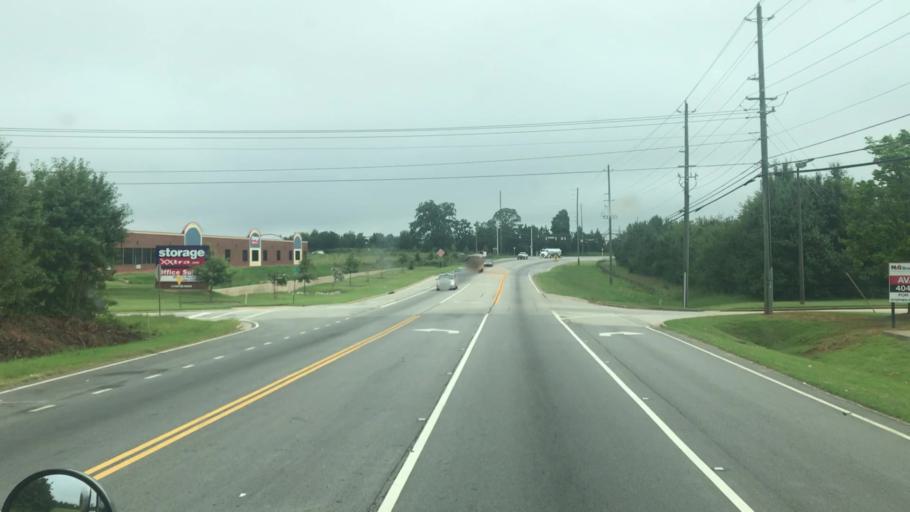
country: US
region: Georgia
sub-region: Henry County
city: McDonough
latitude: 33.4017
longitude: -84.1734
